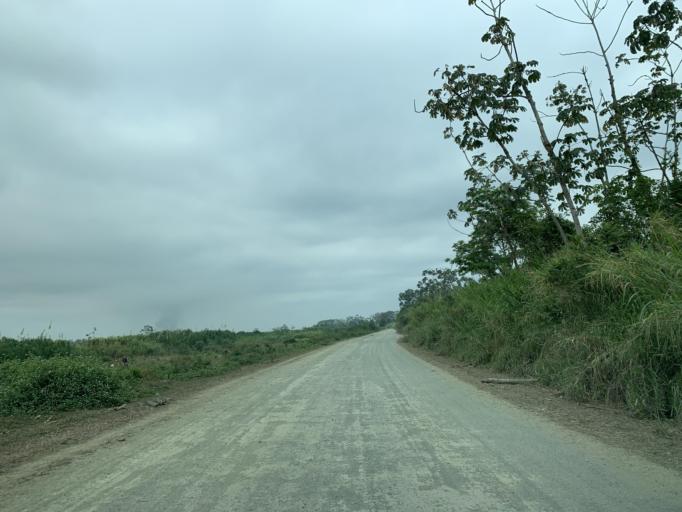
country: EC
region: Canar
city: La Troncal
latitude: -2.3614
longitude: -79.4636
